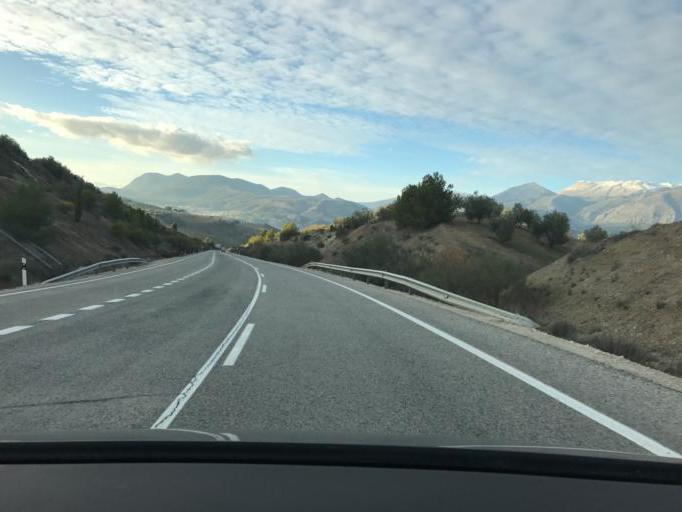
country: ES
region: Andalusia
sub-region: Provincia de Jaen
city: Huelma
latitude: 37.6326
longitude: -3.4027
